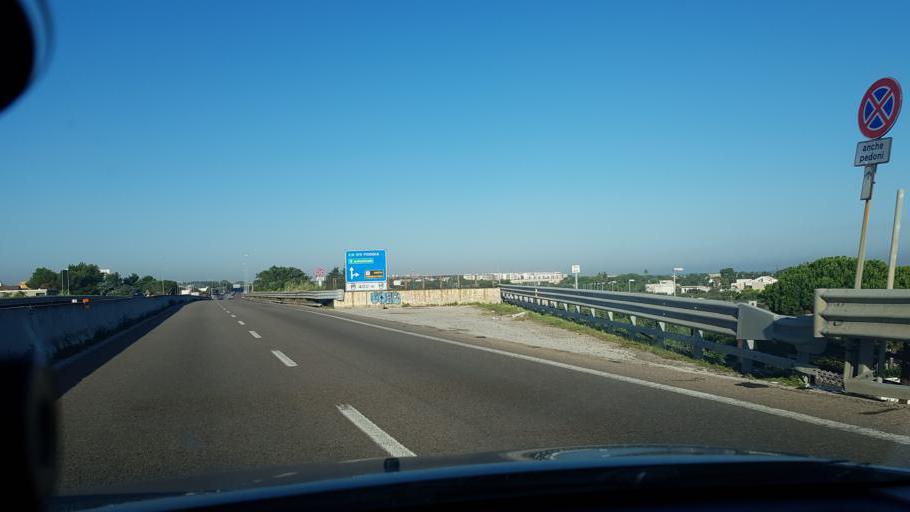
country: IT
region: Apulia
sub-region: Provincia di Bari
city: Parco Scizzo-Parchitello
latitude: 41.0922
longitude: 16.9618
